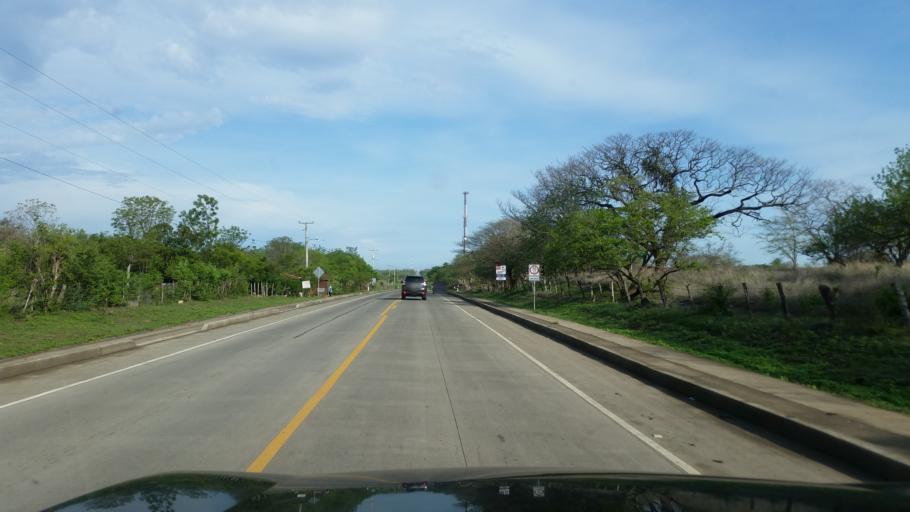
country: NI
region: Managua
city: Carlos Fonseca Amador
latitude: 12.1098
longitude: -86.5965
